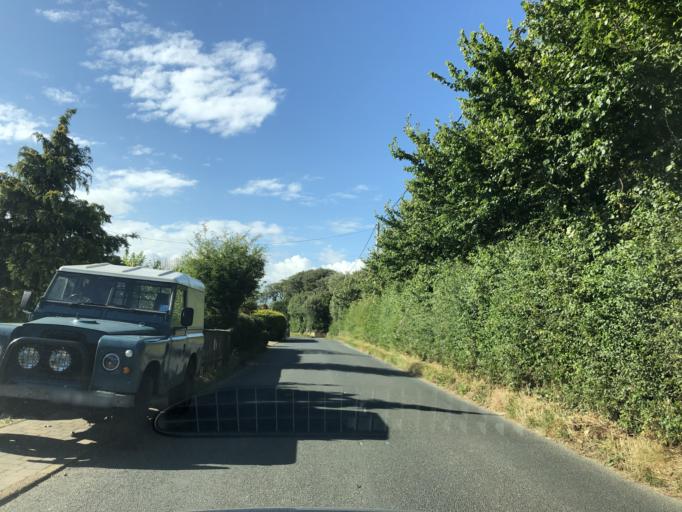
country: GB
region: England
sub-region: Isle of Wight
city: Shalfleet
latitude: 50.6958
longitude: -1.4326
